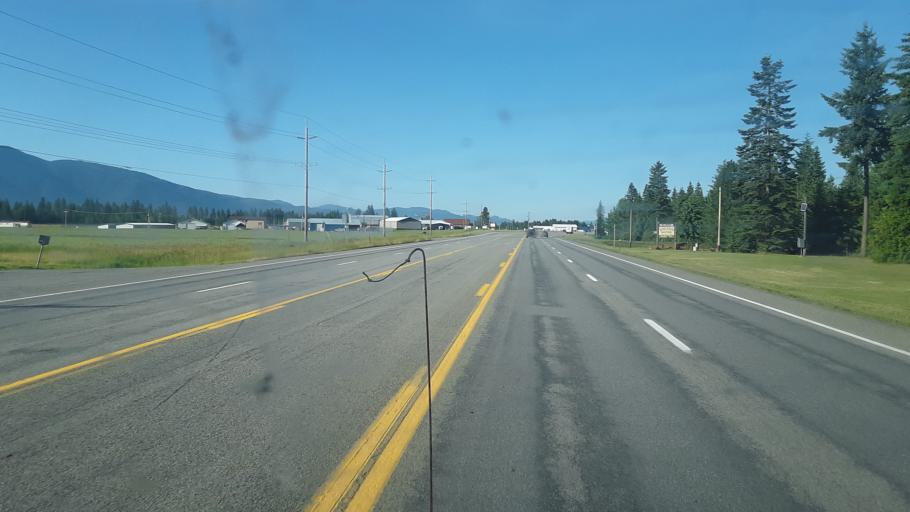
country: US
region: Idaho
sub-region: Boundary County
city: Bonners Ferry
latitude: 48.7279
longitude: -116.3021
